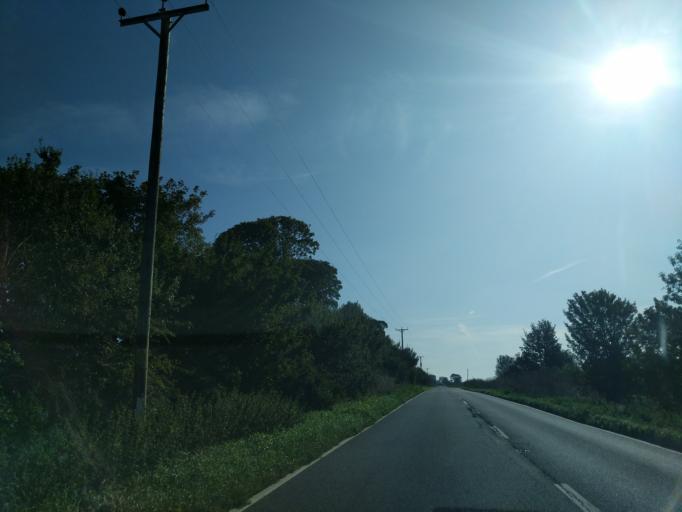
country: GB
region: England
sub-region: Lincolnshire
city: Bourne
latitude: 52.7720
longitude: -0.3052
